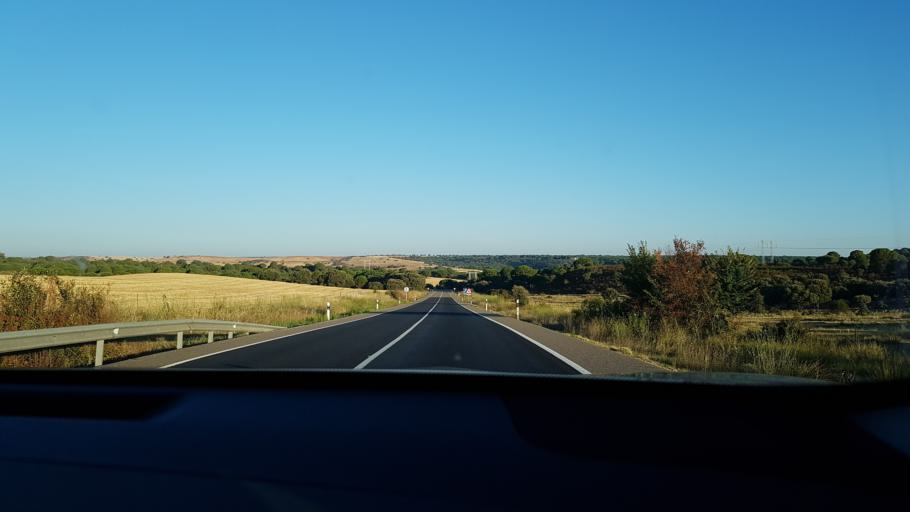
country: ES
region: Castille and Leon
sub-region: Provincia de Zamora
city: Roales
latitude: 41.5285
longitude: -5.8148
